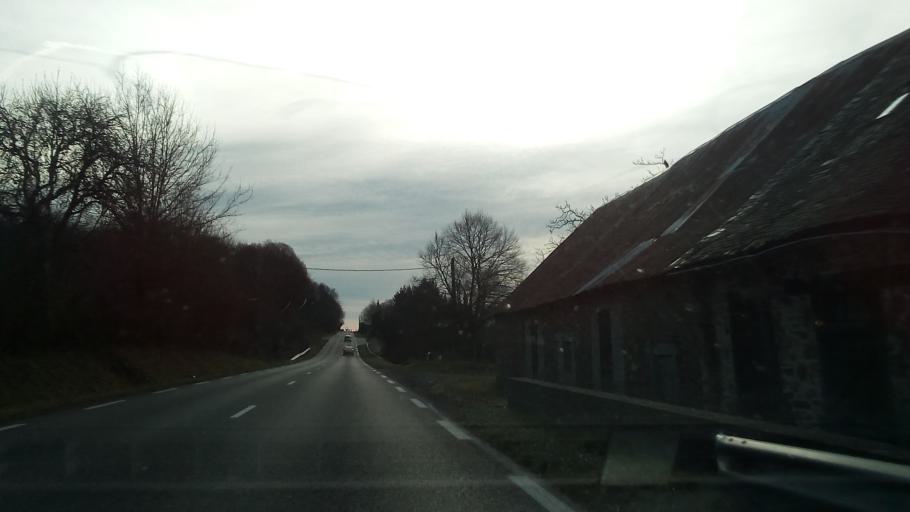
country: FR
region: Limousin
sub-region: Departement de la Correze
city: Seilhac
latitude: 45.3521
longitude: 1.7358
